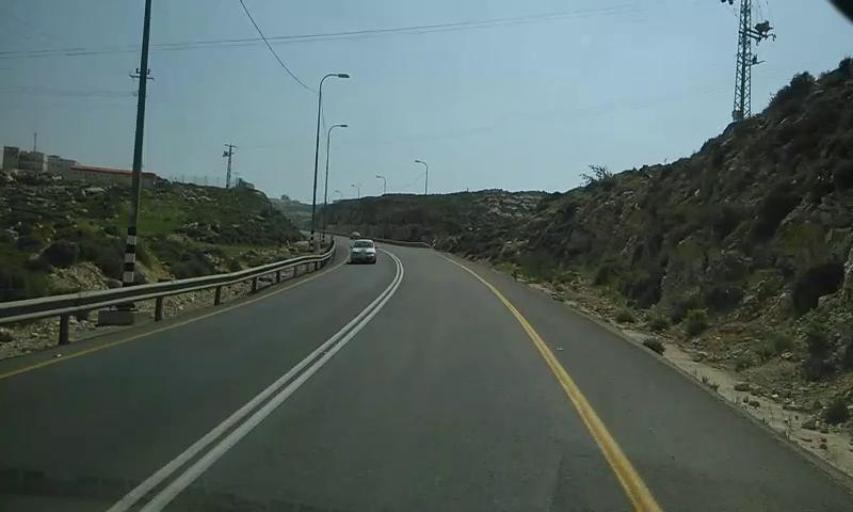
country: PS
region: West Bank
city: Jaba`
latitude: 31.8689
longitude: 35.2580
